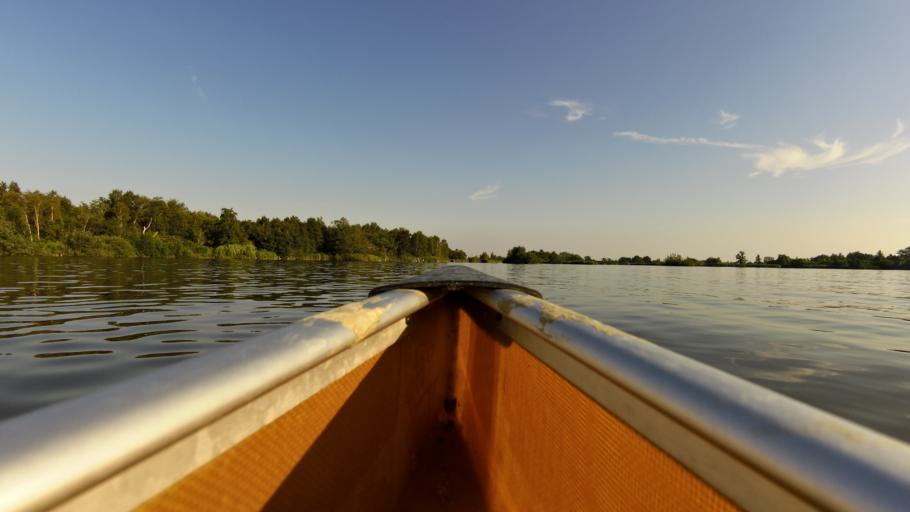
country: NL
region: South Holland
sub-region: Gemeente Nieuwkoop
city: Nieuwkoop
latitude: 52.1387
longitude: 4.7729
